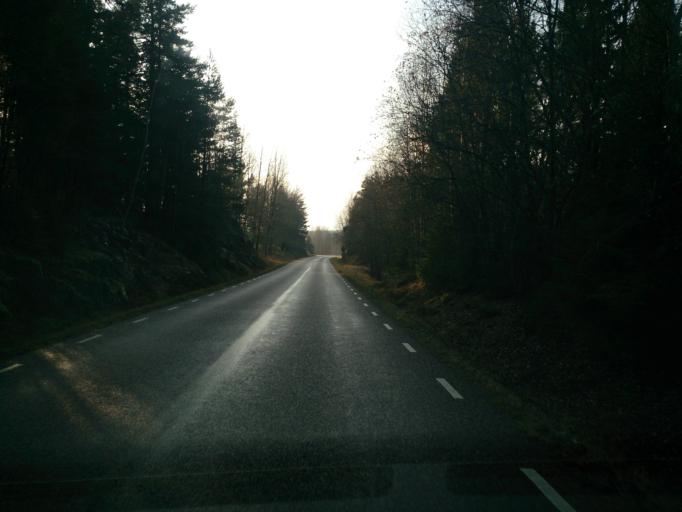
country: SE
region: OEstergoetland
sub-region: Atvidabergs Kommun
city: Atvidaberg
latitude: 58.2467
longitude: 16.0132
